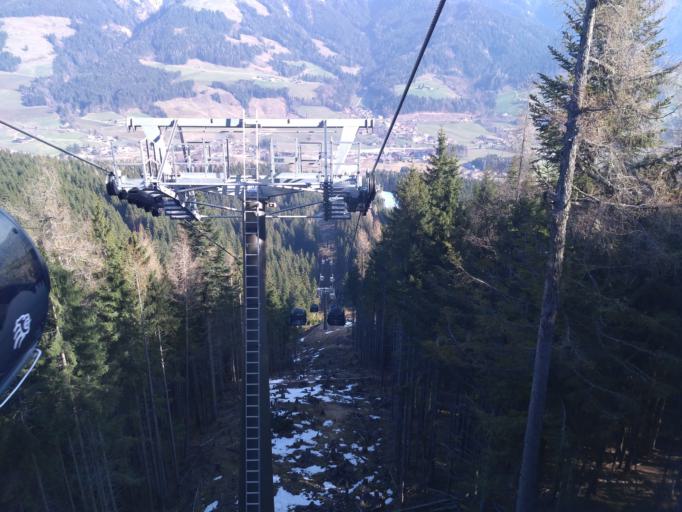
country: AT
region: Salzburg
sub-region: Politischer Bezirk Zell am See
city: Leogang
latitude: 47.4231
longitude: 12.7312
